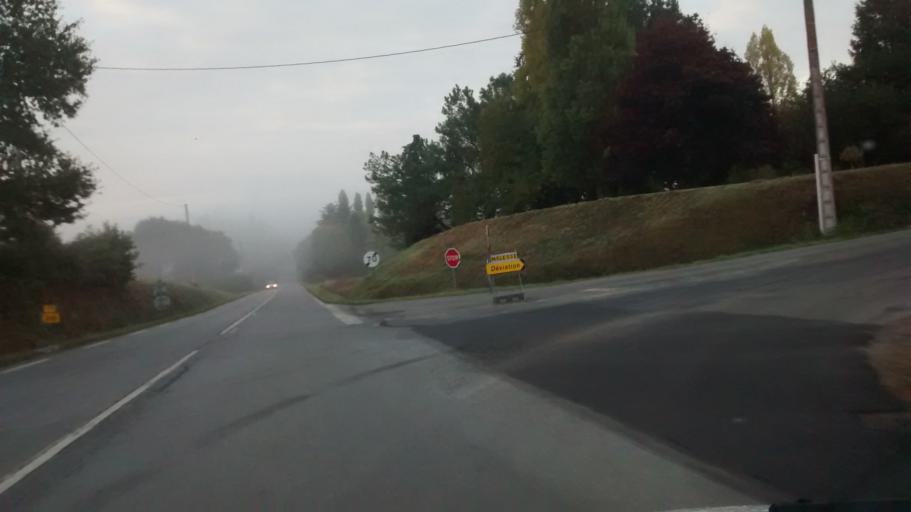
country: FR
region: Brittany
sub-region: Departement d'Ille-et-Vilaine
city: Chevaigne
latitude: 48.1995
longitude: -1.6266
